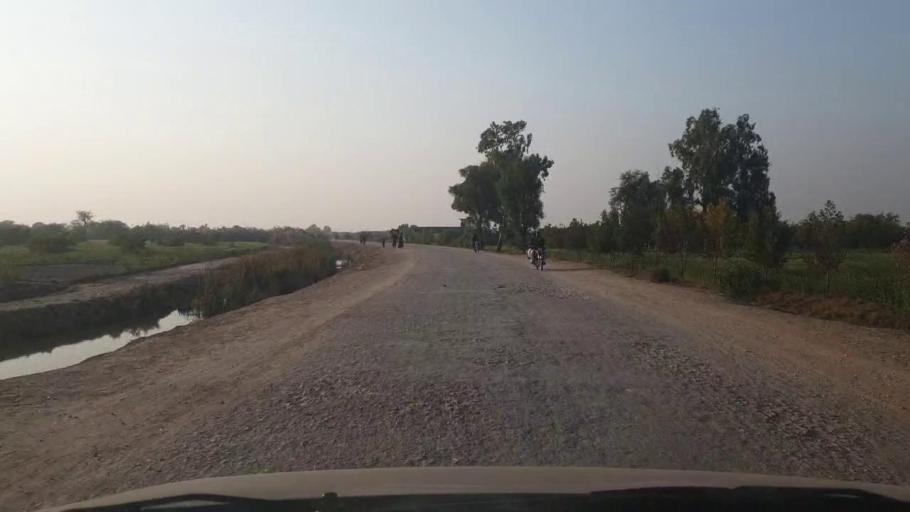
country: PK
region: Sindh
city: Mirwah Gorchani
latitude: 25.3714
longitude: 69.1289
